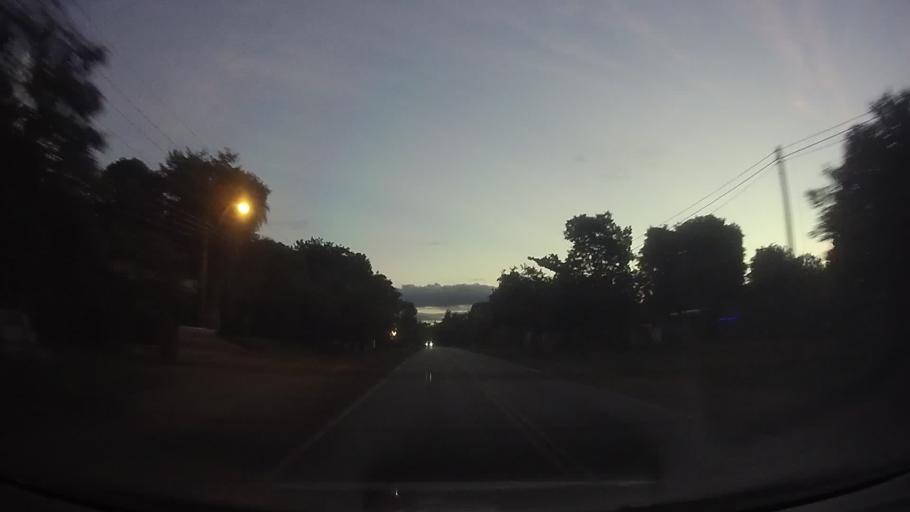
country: PY
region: Central
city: Itaugua
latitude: -25.4026
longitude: -57.3583
